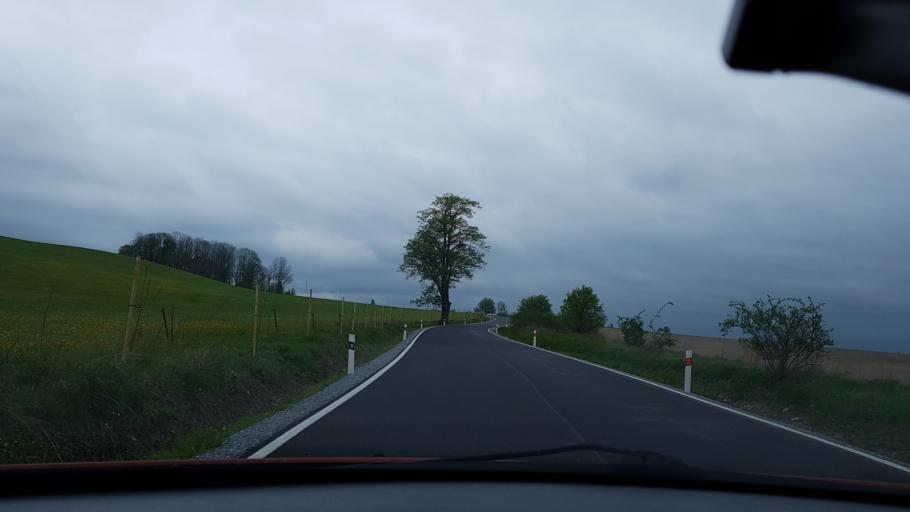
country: PL
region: Opole Voivodeship
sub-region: Powiat nyski
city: Kamienica
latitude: 50.4330
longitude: 16.9487
